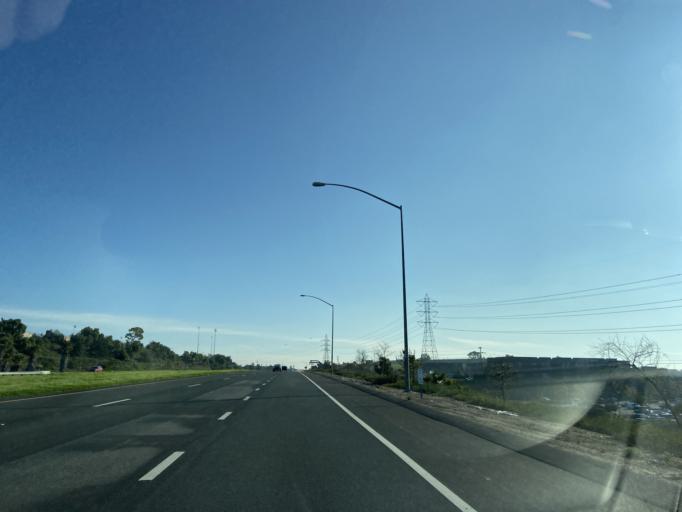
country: US
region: California
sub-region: San Diego County
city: Bonita
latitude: 32.6454
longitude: -116.9711
